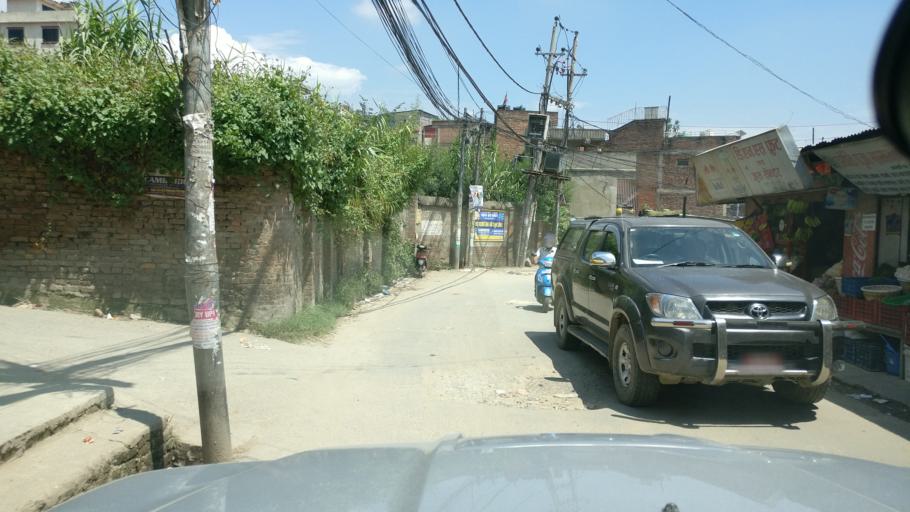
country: NP
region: Central Region
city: Kirtipur
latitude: 27.6933
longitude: 85.2799
